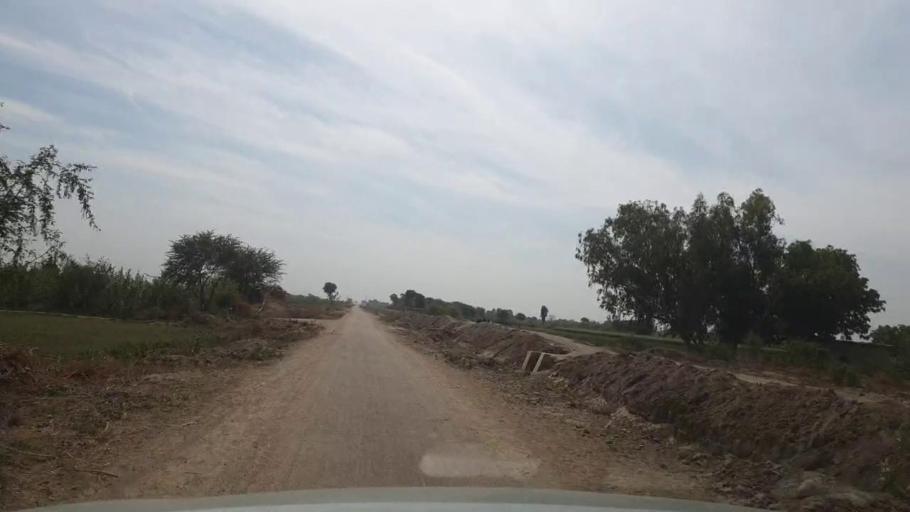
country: PK
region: Sindh
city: Nabisar
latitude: 25.0732
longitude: 69.5790
